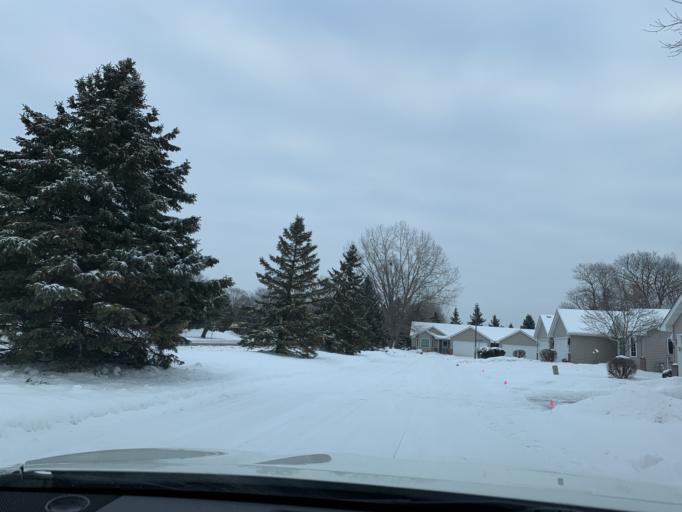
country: US
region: Minnesota
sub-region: Anoka County
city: Coon Rapids
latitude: 45.1625
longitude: -93.2903
